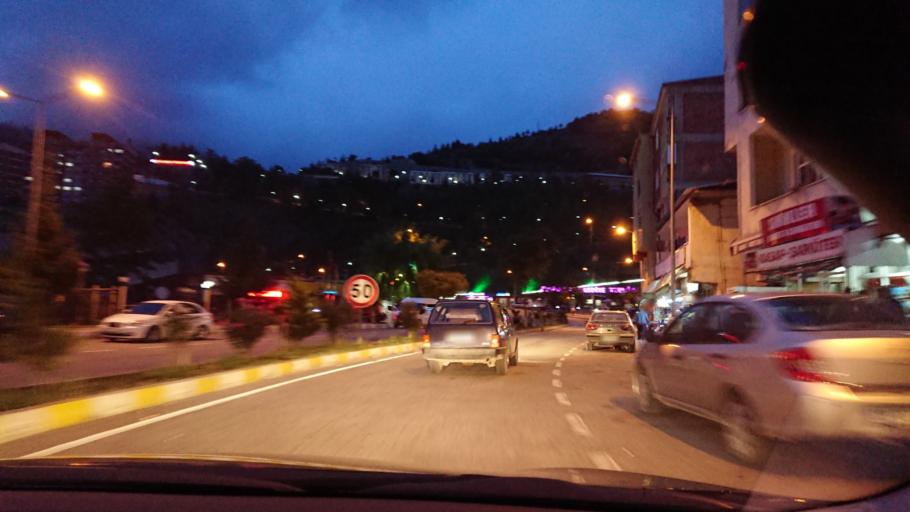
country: TR
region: Gumushane
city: Kurtun
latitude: 40.6701
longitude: 39.1394
